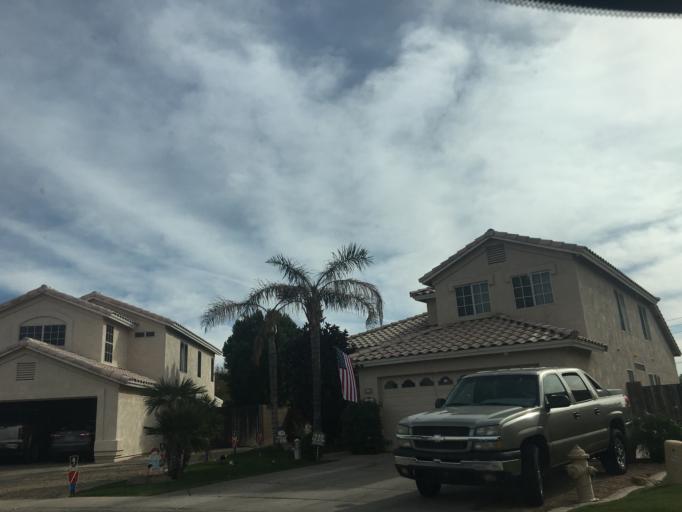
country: US
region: Arizona
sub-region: Maricopa County
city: Gilbert
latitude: 33.3505
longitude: -111.7967
